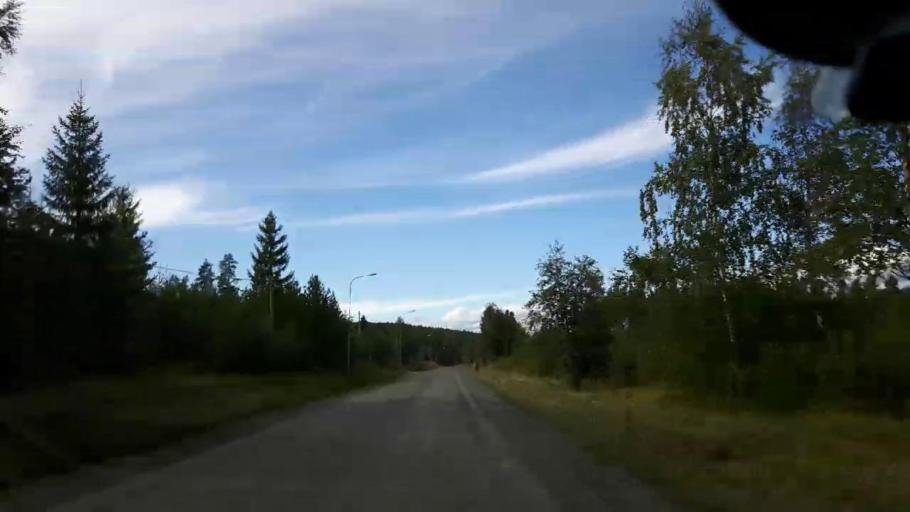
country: SE
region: Jaemtland
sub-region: Ragunda Kommun
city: Hammarstrand
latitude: 63.1413
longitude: 15.9157
